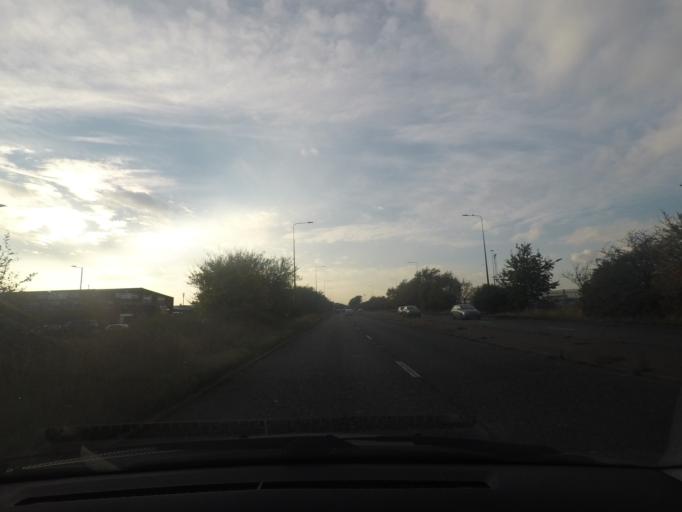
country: GB
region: England
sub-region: North East Lincolnshire
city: Grimsby
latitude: 53.5738
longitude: -0.0861
